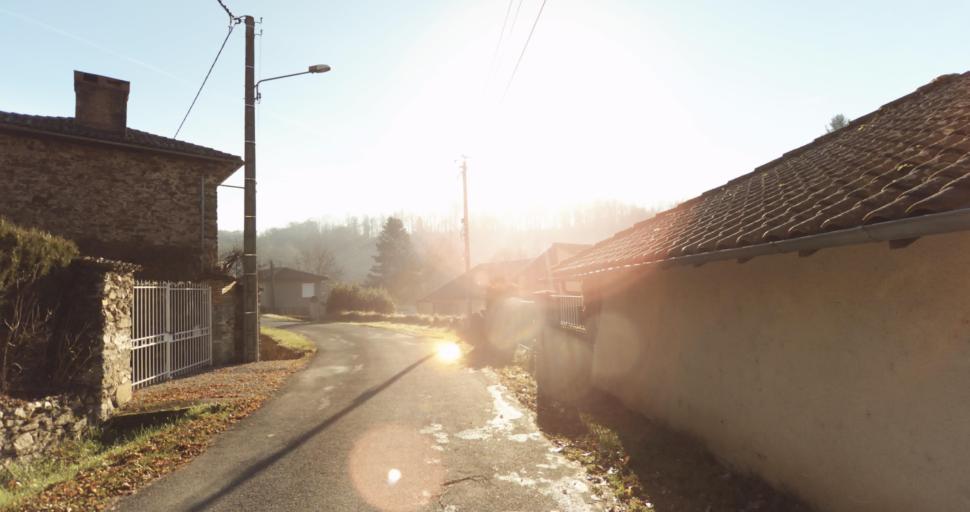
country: FR
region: Limousin
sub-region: Departement de la Haute-Vienne
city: Aixe-sur-Vienne
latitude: 45.7997
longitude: 1.1548
